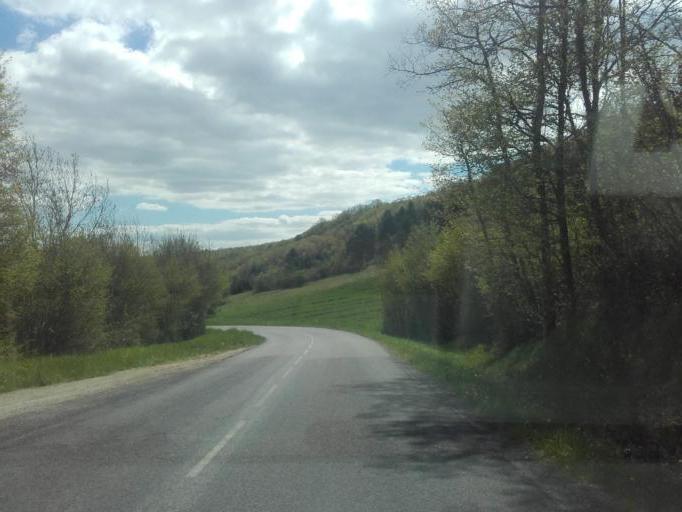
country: FR
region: Bourgogne
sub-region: Departement de la Cote-d'Or
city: Meursault
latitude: 47.0145
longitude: 4.7223
